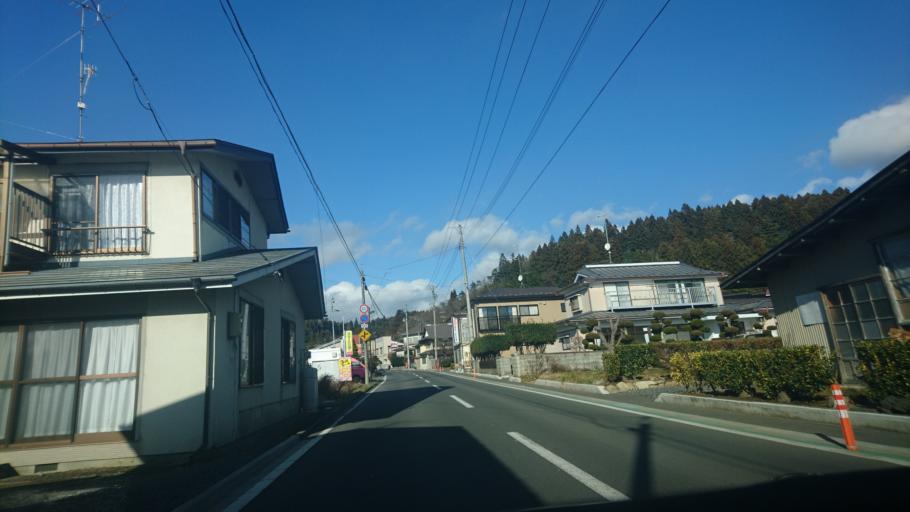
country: JP
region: Iwate
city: Mizusawa
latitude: 39.0531
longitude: 141.3663
